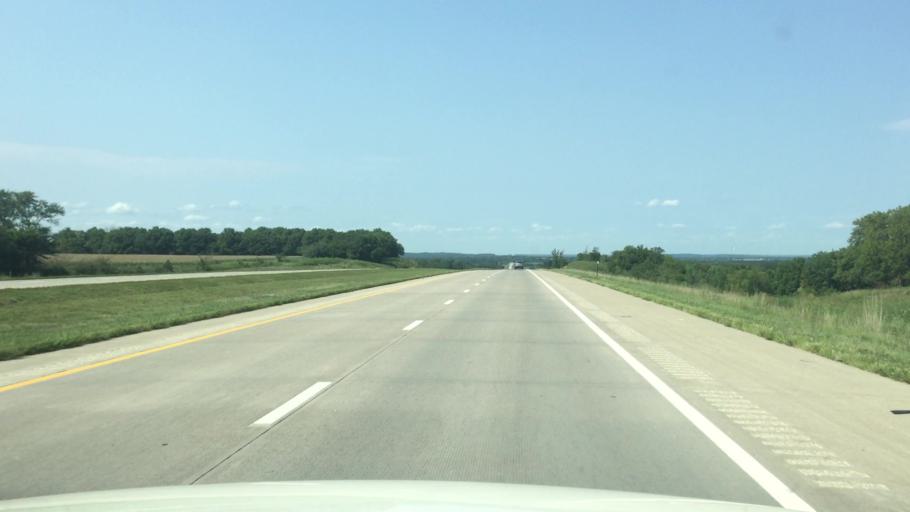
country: US
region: Kansas
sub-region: Linn County
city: Pleasanton
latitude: 38.1109
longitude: -94.7133
